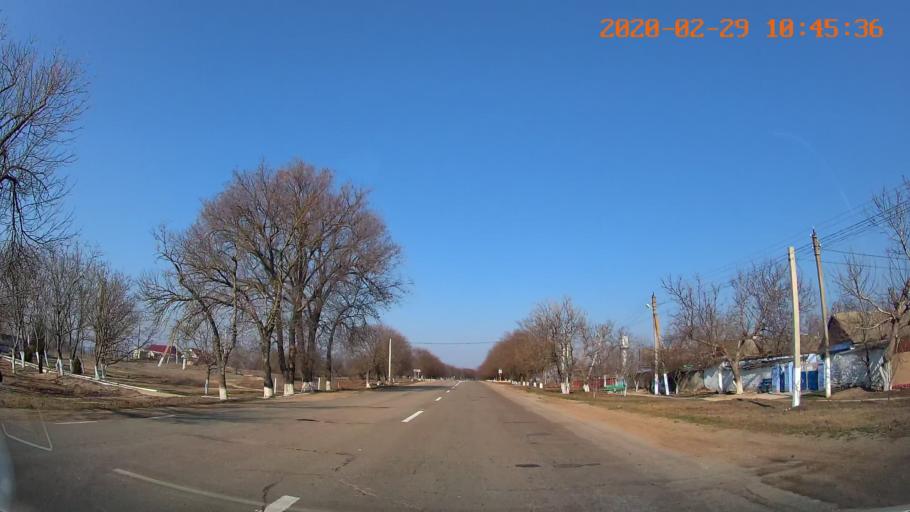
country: MD
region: Telenesti
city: Grigoriopol
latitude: 47.0771
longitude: 29.3815
